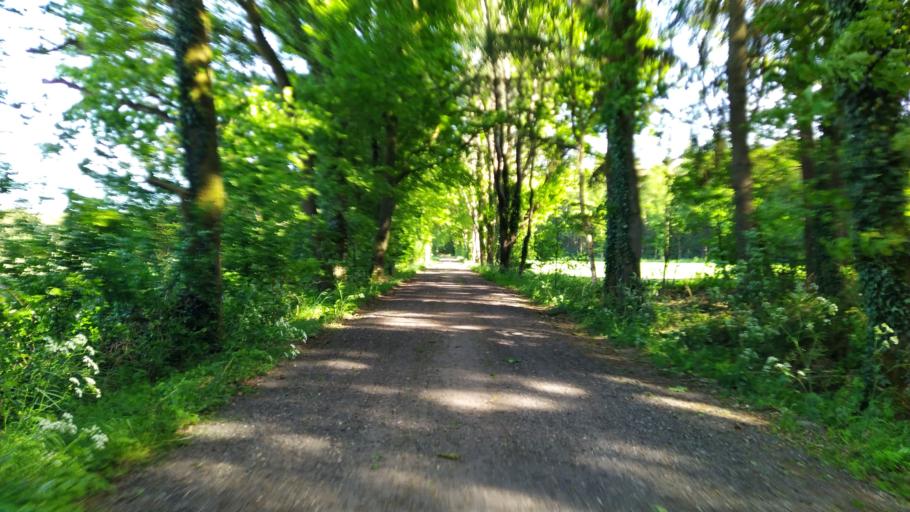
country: DE
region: Lower Saxony
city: Ahlerstedt
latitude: 53.4223
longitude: 9.4798
